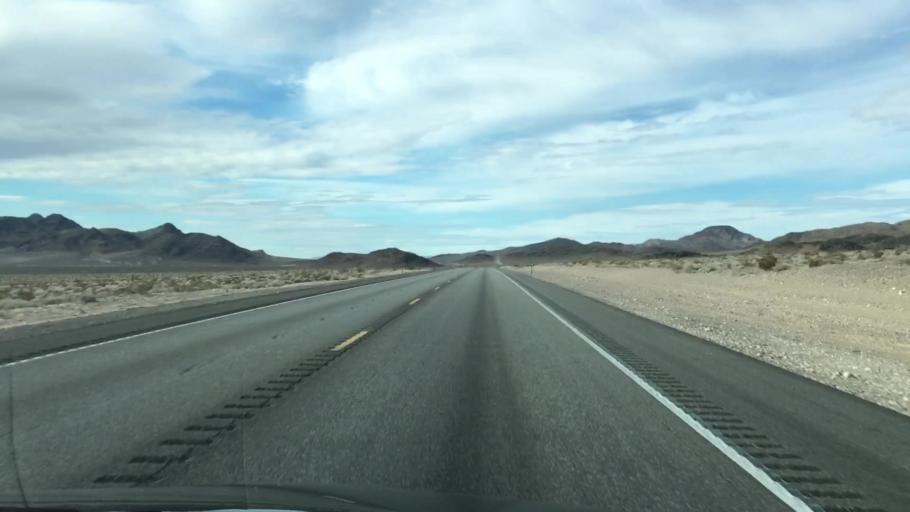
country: US
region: Nevada
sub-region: Nye County
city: Pahrump
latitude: 36.6166
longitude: -116.2845
